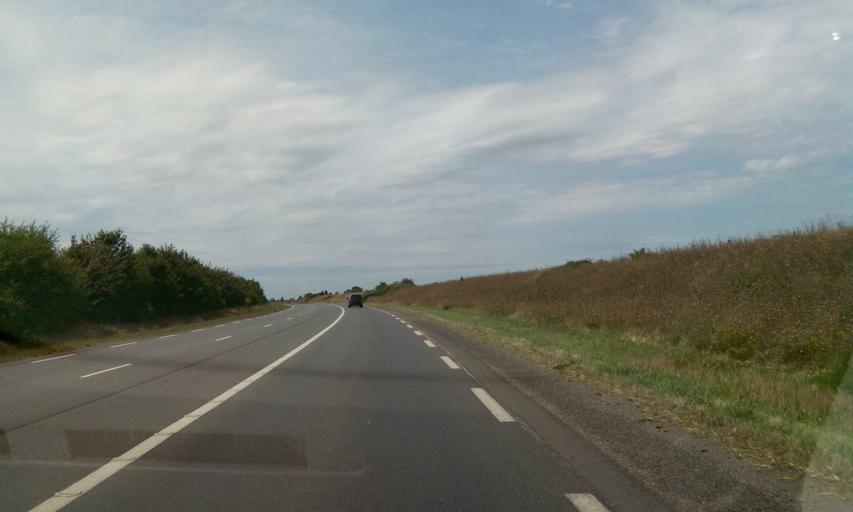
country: FR
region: Poitou-Charentes
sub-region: Departement des Deux-Sevres
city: Mougon
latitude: 46.3013
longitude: -0.3276
